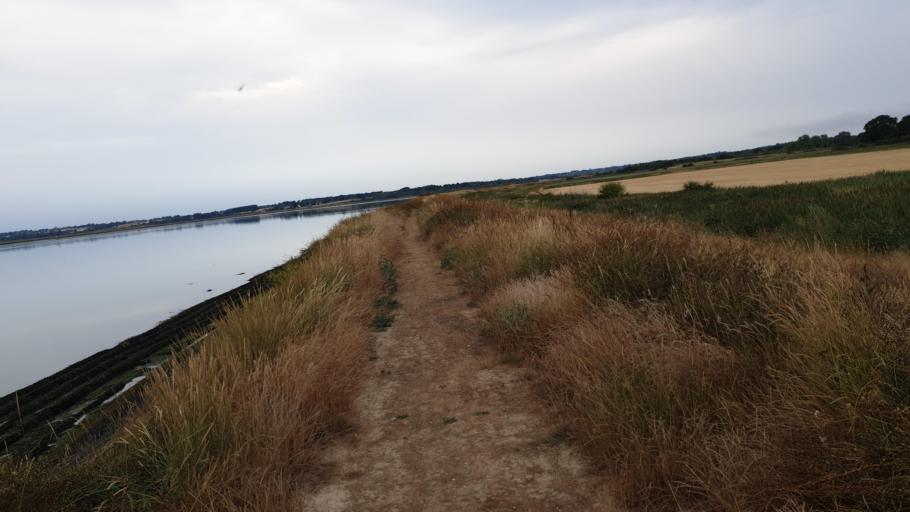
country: GB
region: England
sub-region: Essex
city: Brightlingsea
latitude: 51.8201
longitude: 0.9913
